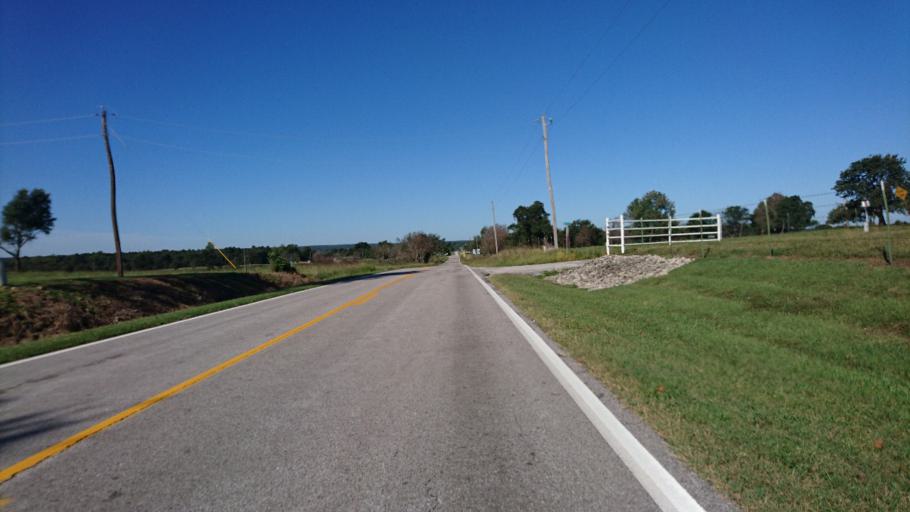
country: US
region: Missouri
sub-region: Greene County
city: Ash Grove
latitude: 37.1940
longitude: -93.6658
